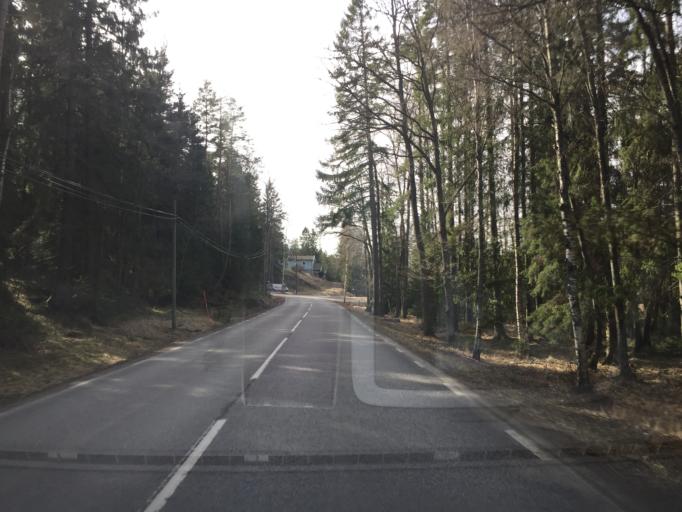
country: SE
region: Stockholm
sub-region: Haninge Kommun
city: Jordbro
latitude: 59.1108
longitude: 17.9989
